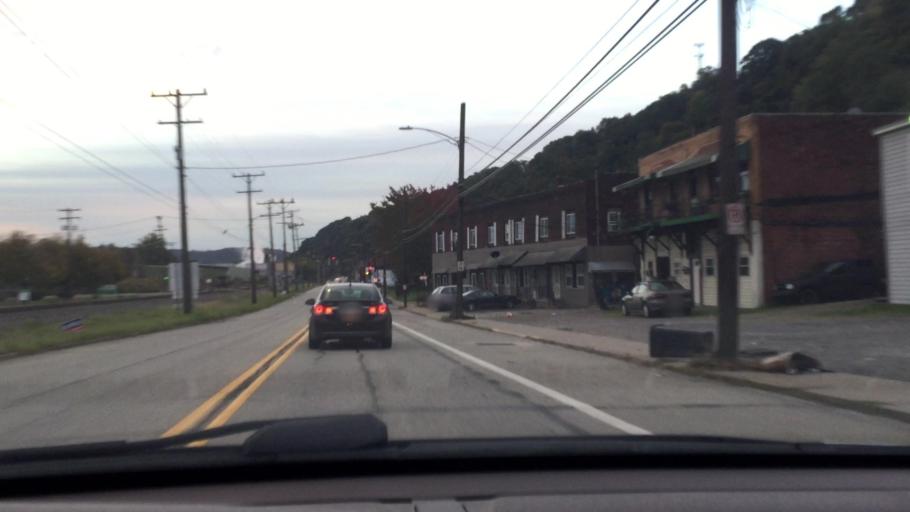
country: US
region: Pennsylvania
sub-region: Westmoreland County
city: Arnold
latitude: 40.5783
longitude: -79.7787
